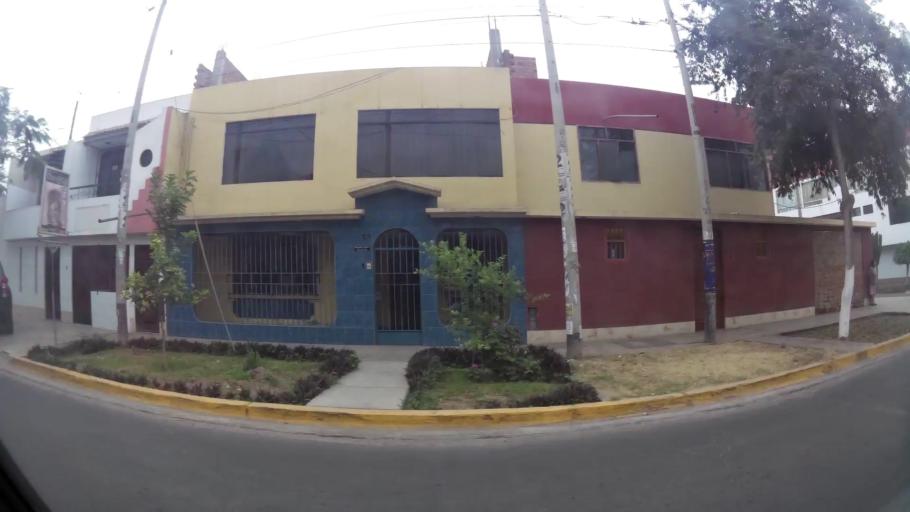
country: PE
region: La Libertad
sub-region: Provincia de Trujillo
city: Trujillo
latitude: -8.1092
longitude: -79.0401
